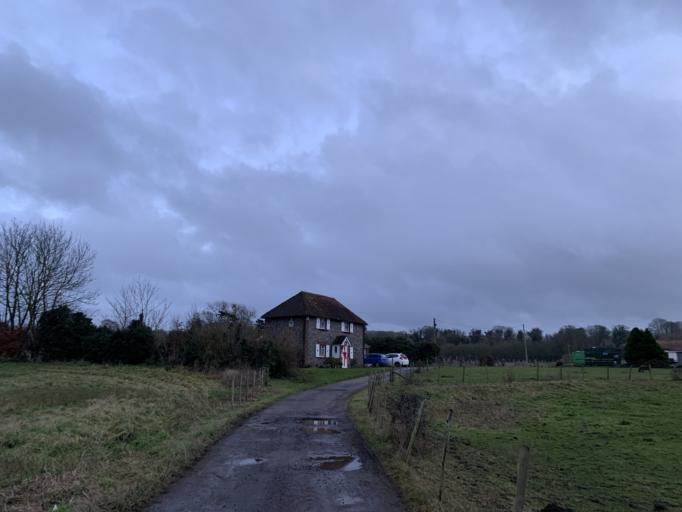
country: GB
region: England
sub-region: Kent
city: Eynsford
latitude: 51.3640
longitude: 0.1981
